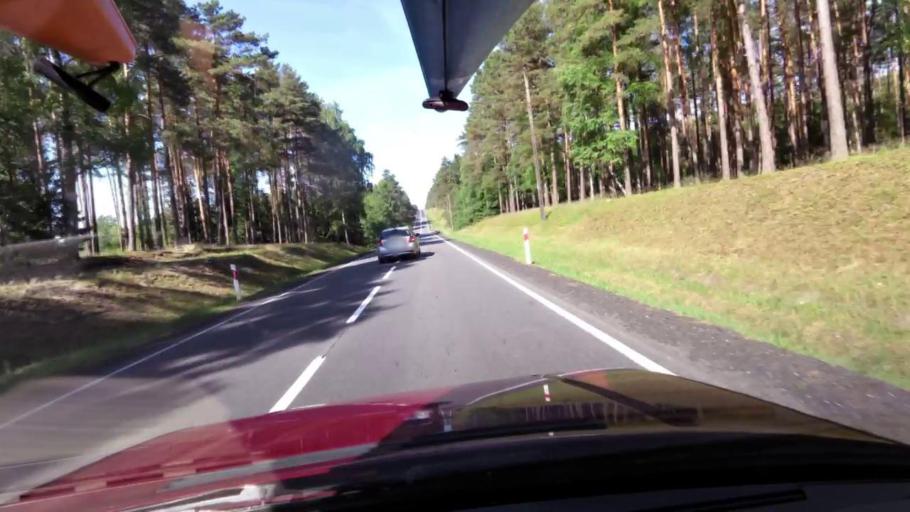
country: PL
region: Pomeranian Voivodeship
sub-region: Powiat bytowski
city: Trzebielino
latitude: 54.1550
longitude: 17.0453
